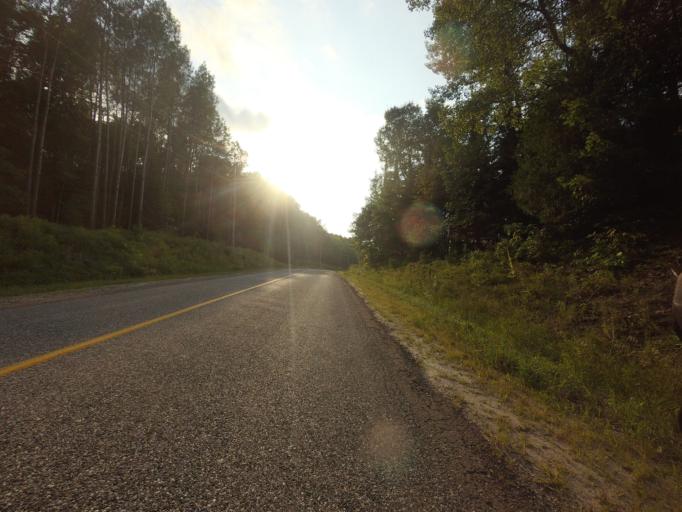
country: CA
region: Ontario
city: Perth
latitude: 44.9652
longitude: -76.7148
